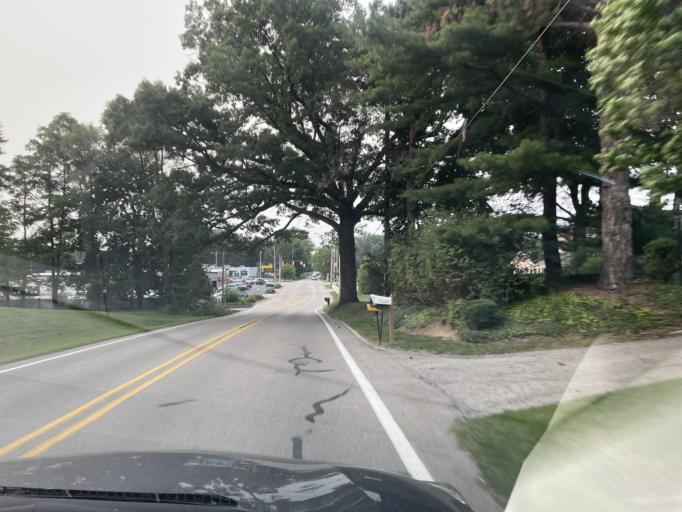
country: US
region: Michigan
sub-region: Kent County
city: Walker
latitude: 42.9703
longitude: -85.7371
